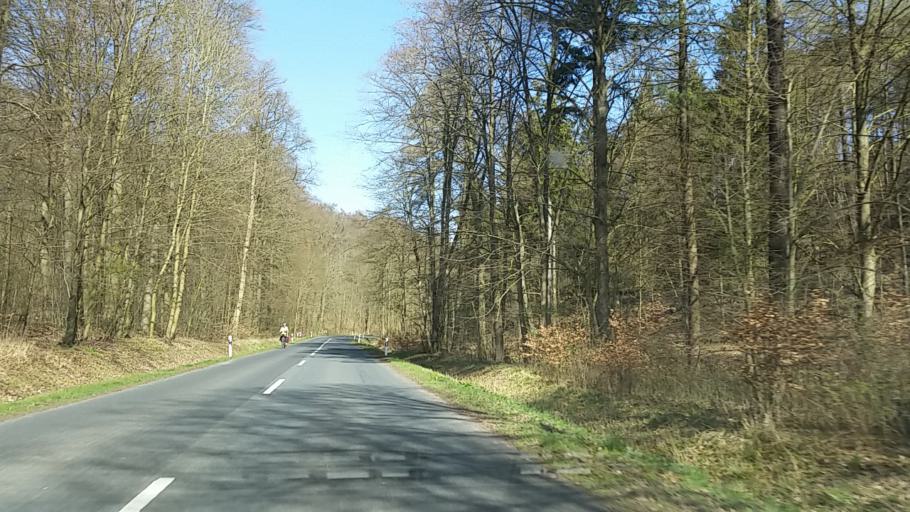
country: DE
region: Lower Saxony
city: Konigslutter am Elm
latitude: 52.2224
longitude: 10.8027
